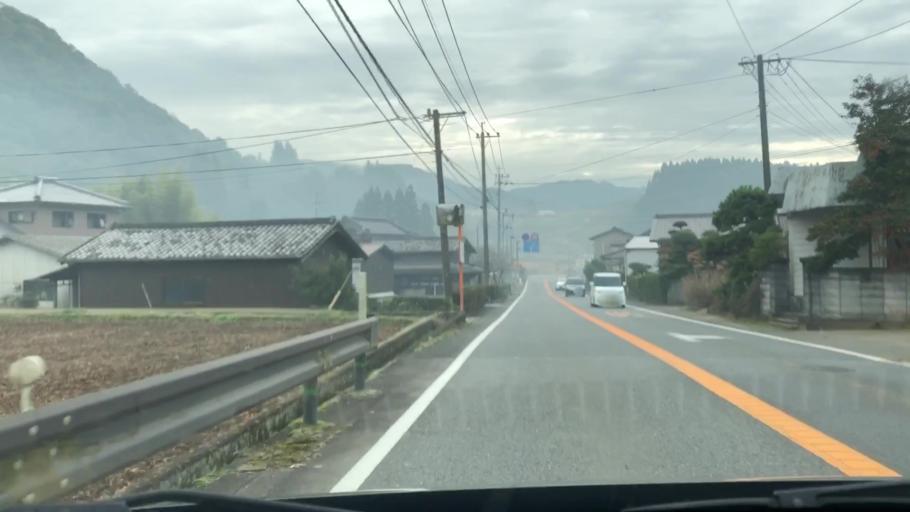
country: JP
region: Oita
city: Usuki
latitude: 33.0186
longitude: 131.6997
